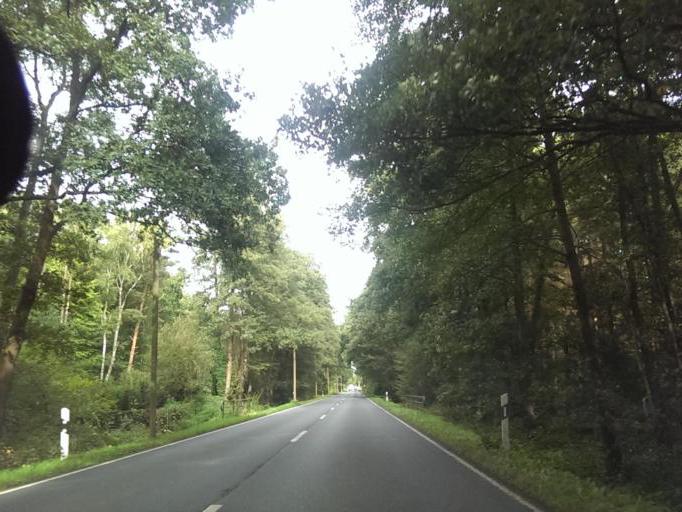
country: DE
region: Lower Saxony
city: Garbsen-Mitte
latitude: 52.4873
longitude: 9.6352
